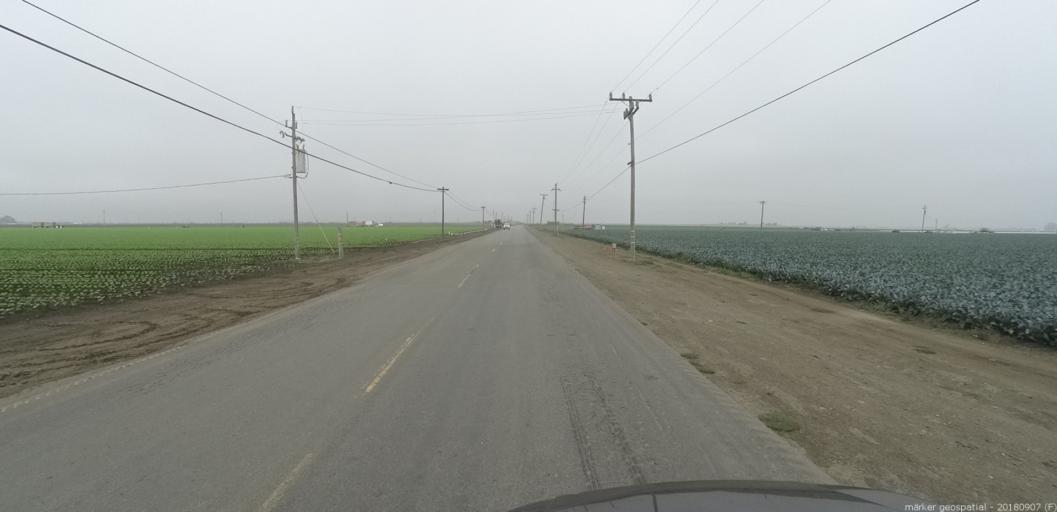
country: US
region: California
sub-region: Monterey County
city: Castroville
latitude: 36.7350
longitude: -121.7589
